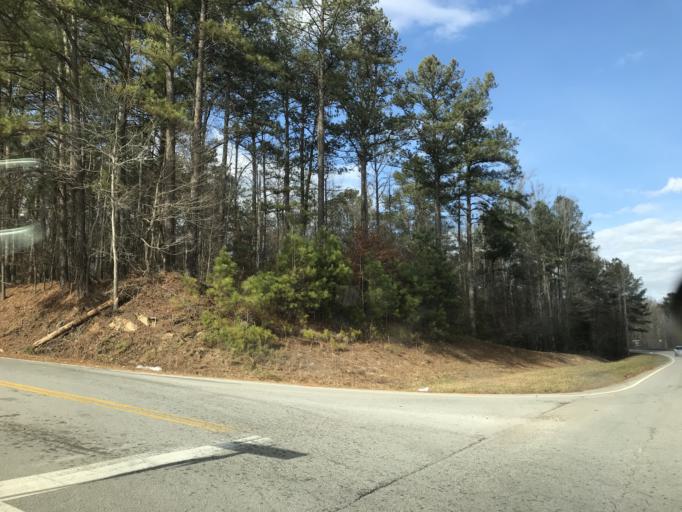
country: US
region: Georgia
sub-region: Douglas County
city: Douglasville
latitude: 33.7976
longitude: -84.8062
